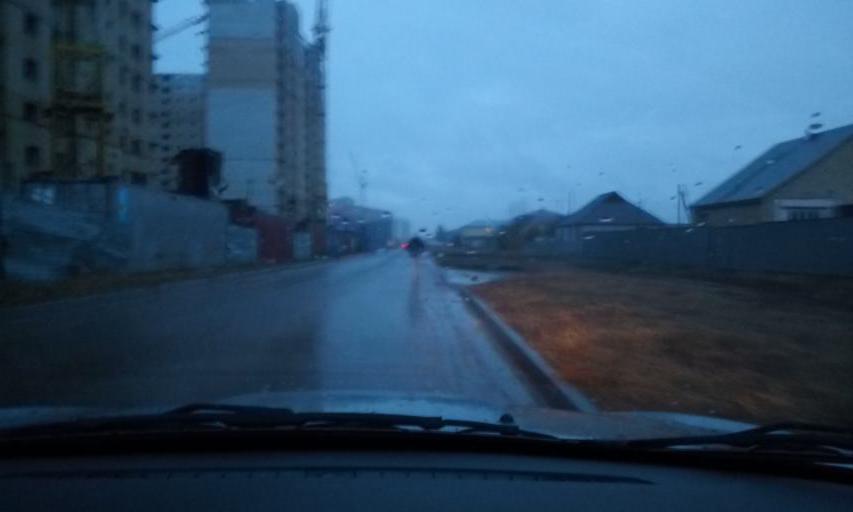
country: KZ
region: Astana Qalasy
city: Astana
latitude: 51.1917
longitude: 71.3391
